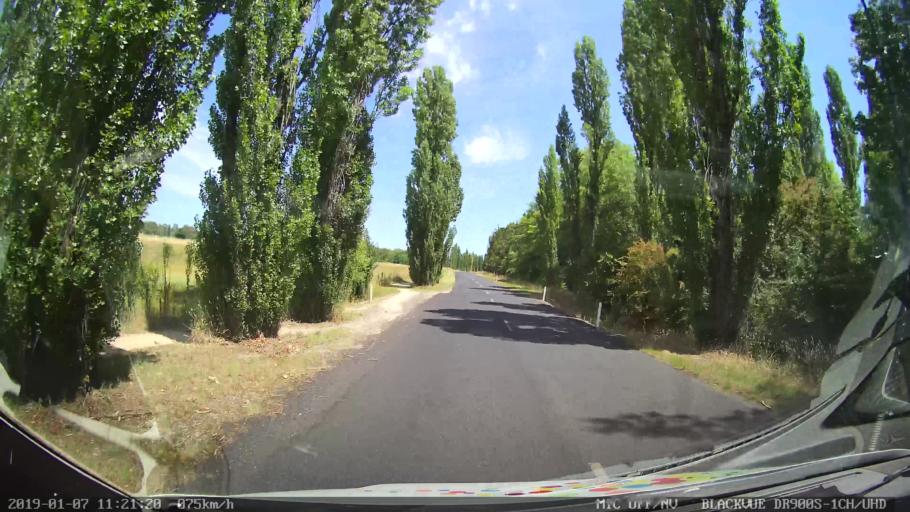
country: AU
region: New South Wales
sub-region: Armidale Dumaresq
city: Armidale
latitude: -30.4942
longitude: 151.6313
